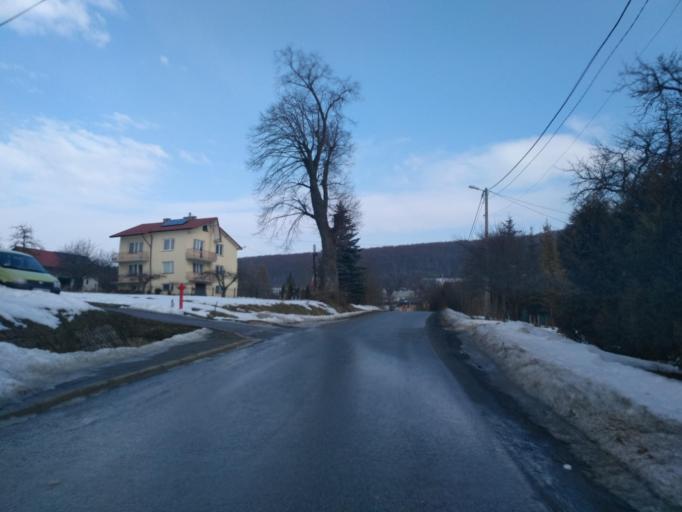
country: PL
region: Subcarpathian Voivodeship
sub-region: Powiat brzozowski
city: Dydnia
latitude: 49.6389
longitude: 22.1850
